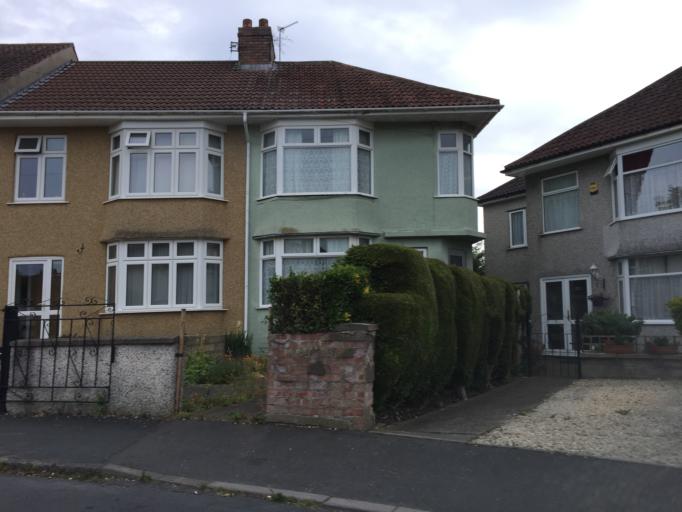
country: GB
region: England
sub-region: South Gloucestershire
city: Stoke Gifford
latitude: 51.5017
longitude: -2.5668
